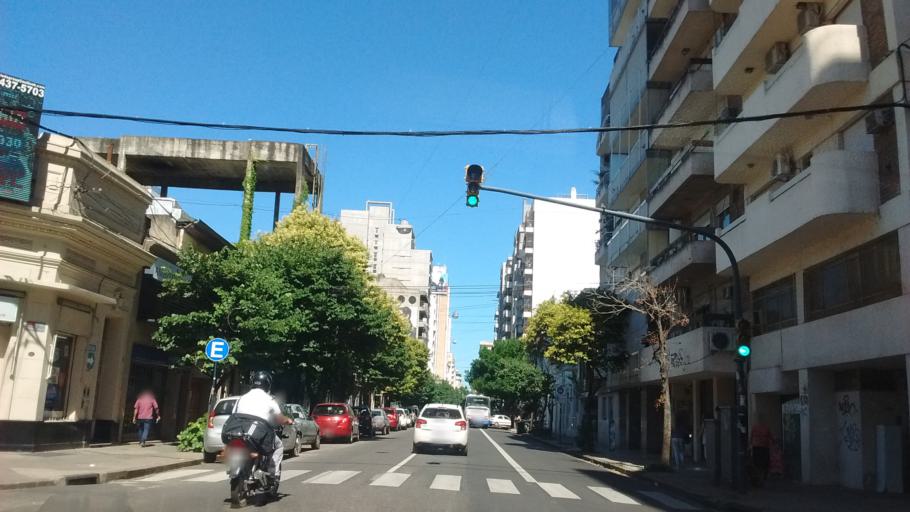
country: AR
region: Santa Fe
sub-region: Departamento de Rosario
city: Rosario
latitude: -32.9430
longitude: -60.6575
